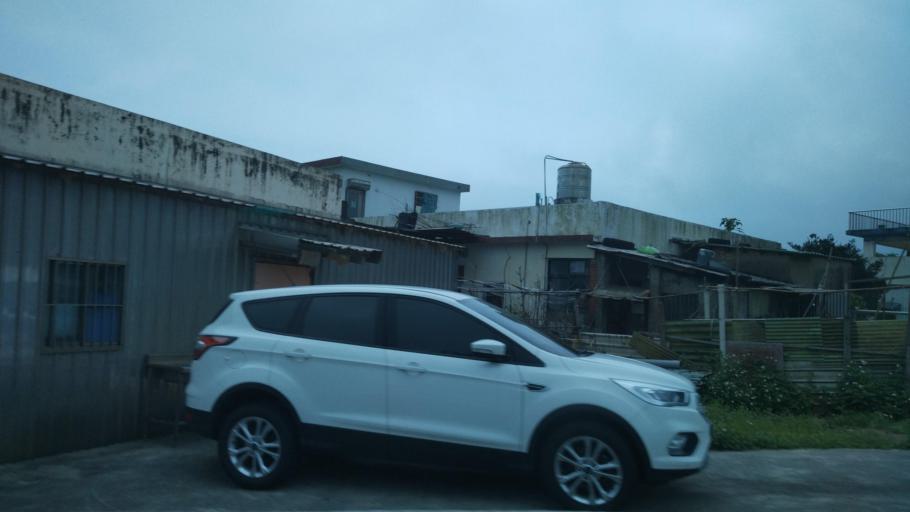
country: TW
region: Taiwan
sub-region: Keelung
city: Keelung
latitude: 25.2162
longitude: 121.6478
